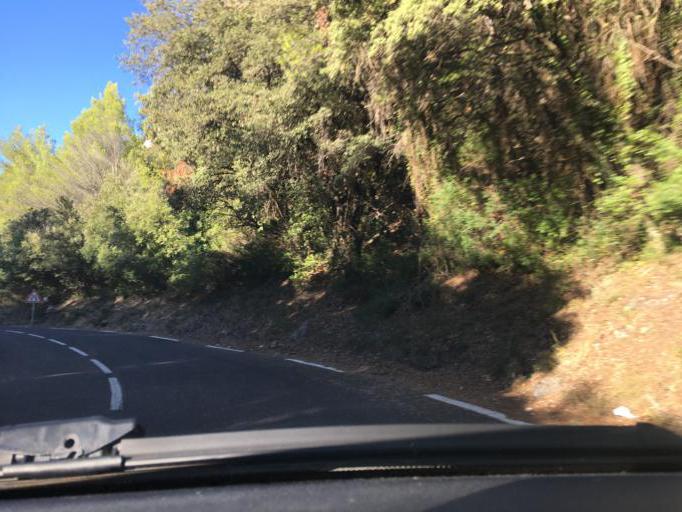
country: FR
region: Provence-Alpes-Cote d'Azur
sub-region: Departement du Var
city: Flayosc
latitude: 43.5808
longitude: 6.4260
